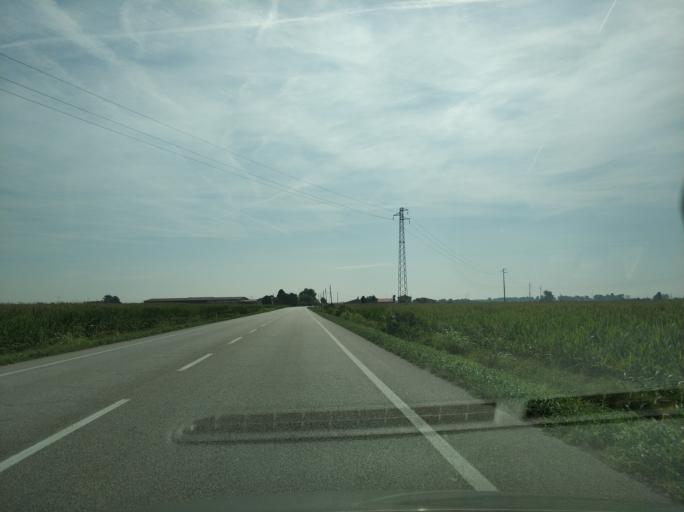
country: IT
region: Veneto
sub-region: Provincia di Padova
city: Correzzola
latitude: 45.2176
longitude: 12.0908
